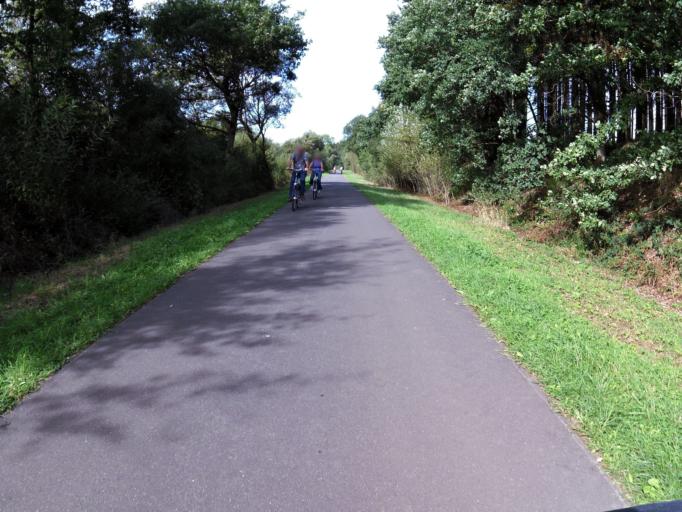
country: DE
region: Rheinland-Pfalz
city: Pronsfeld
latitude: 50.1766
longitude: 6.3162
